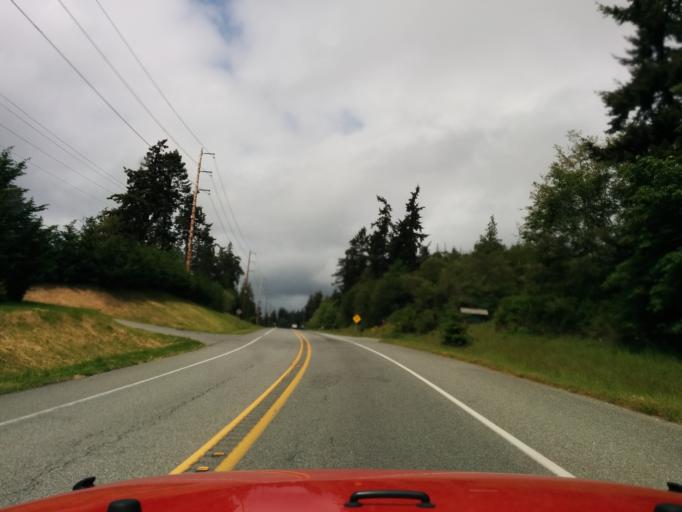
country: US
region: Washington
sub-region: Island County
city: Freeland
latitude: 48.0179
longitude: -122.5489
